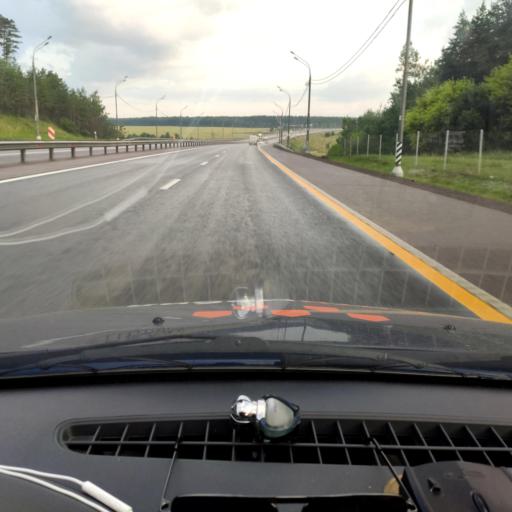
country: RU
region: Lipetsk
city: Zadonsk
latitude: 52.3395
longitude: 38.9662
